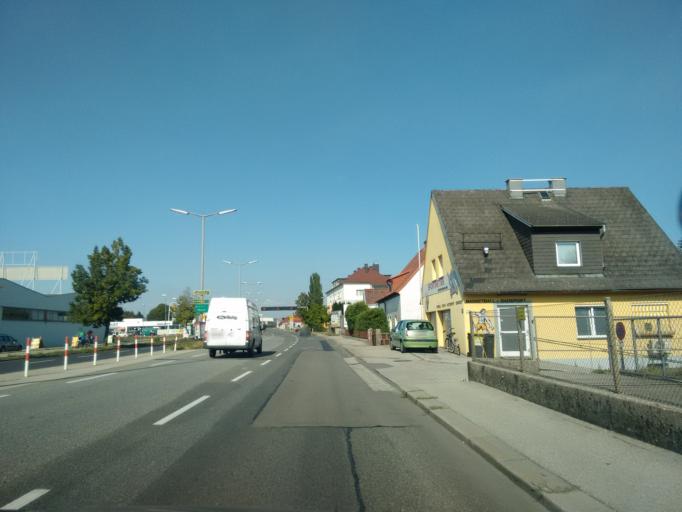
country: AT
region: Upper Austria
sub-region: Wels Stadt
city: Wels
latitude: 48.1742
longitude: 14.0549
